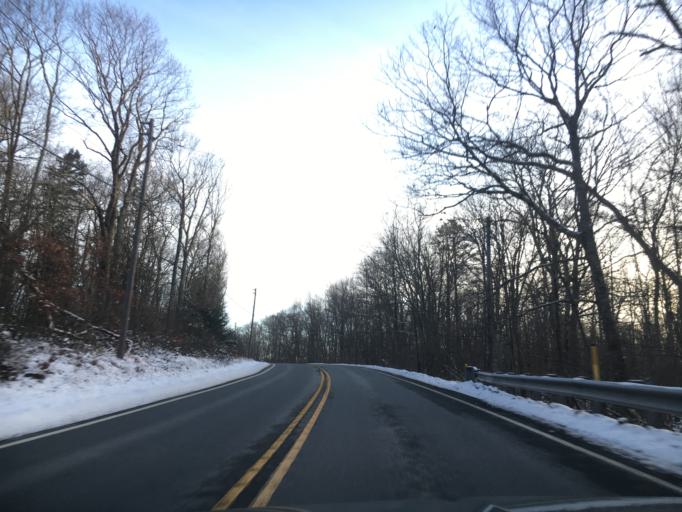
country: US
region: Pennsylvania
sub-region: Pike County
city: Hemlock Farms
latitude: 41.2732
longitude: -75.0870
